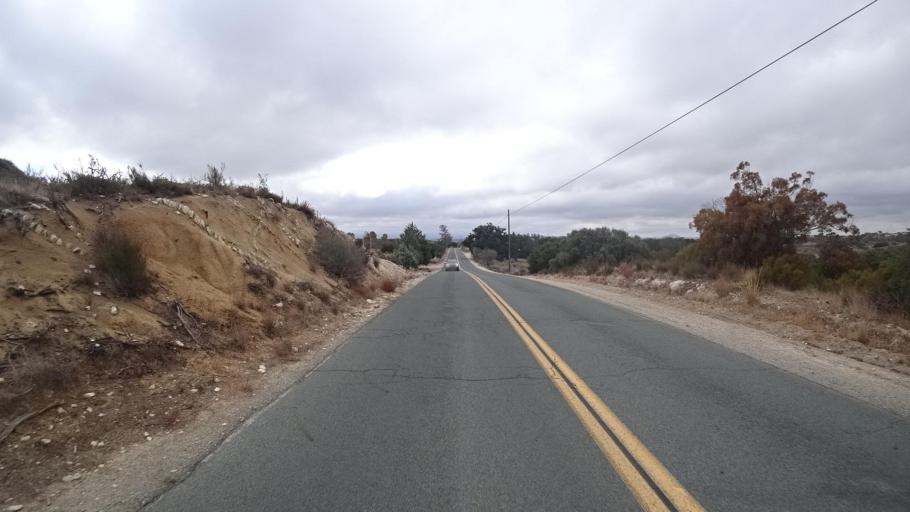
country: US
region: California
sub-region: San Diego County
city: Campo
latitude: 32.6325
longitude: -116.3201
